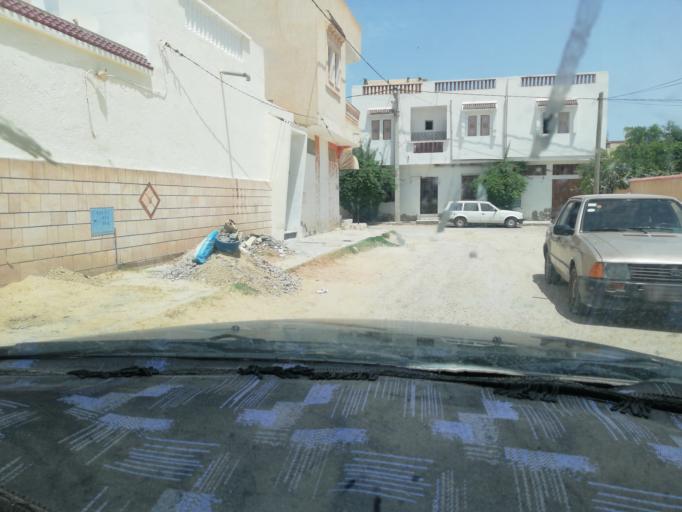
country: TN
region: Qabis
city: Matmata
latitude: 33.6193
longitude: 10.2839
